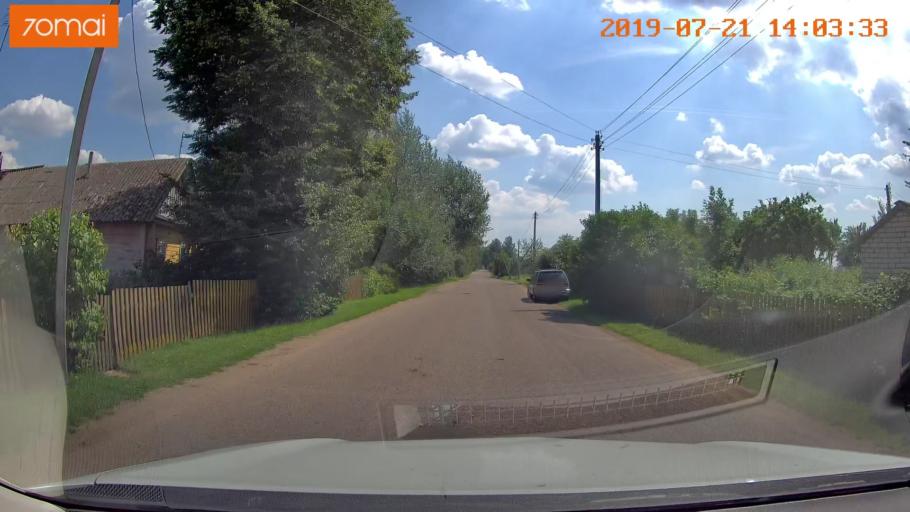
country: BY
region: Grodnenskaya
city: Lyubcha
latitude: 53.7282
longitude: 26.0919
